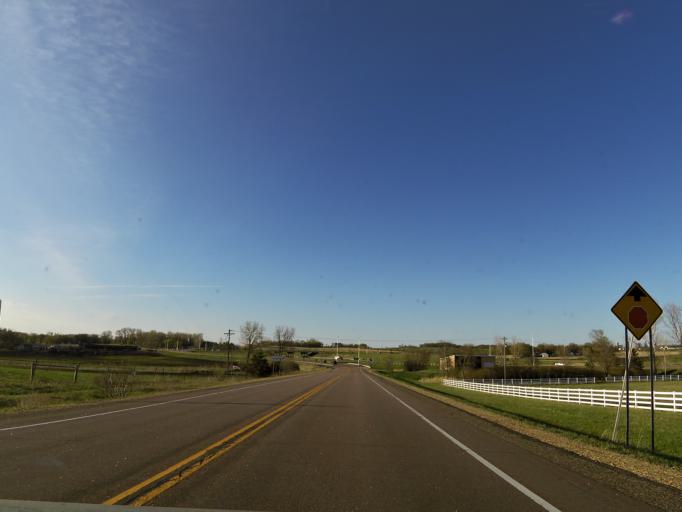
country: US
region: Minnesota
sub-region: Goodhue County
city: Cannon Falls
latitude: 44.5966
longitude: -92.9935
